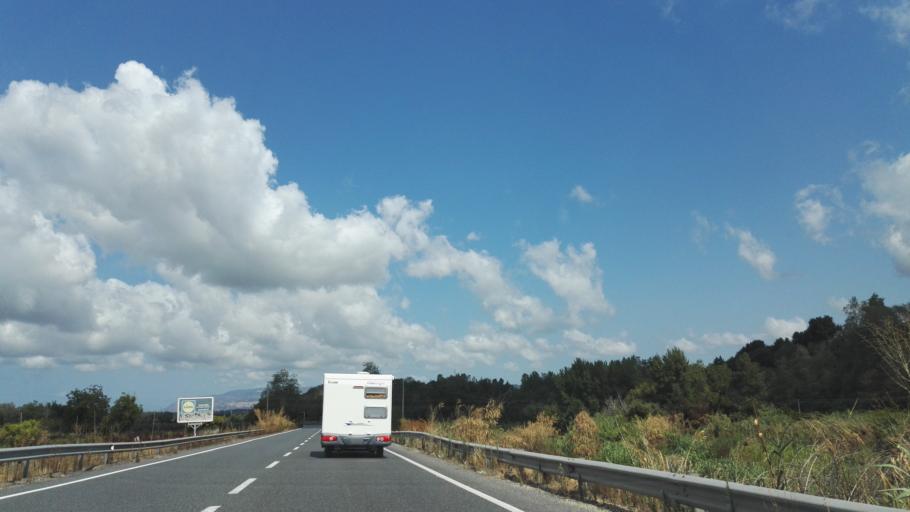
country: IT
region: Calabria
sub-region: Provincia di Reggio Calabria
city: Melicucco
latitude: 38.4450
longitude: 16.0393
